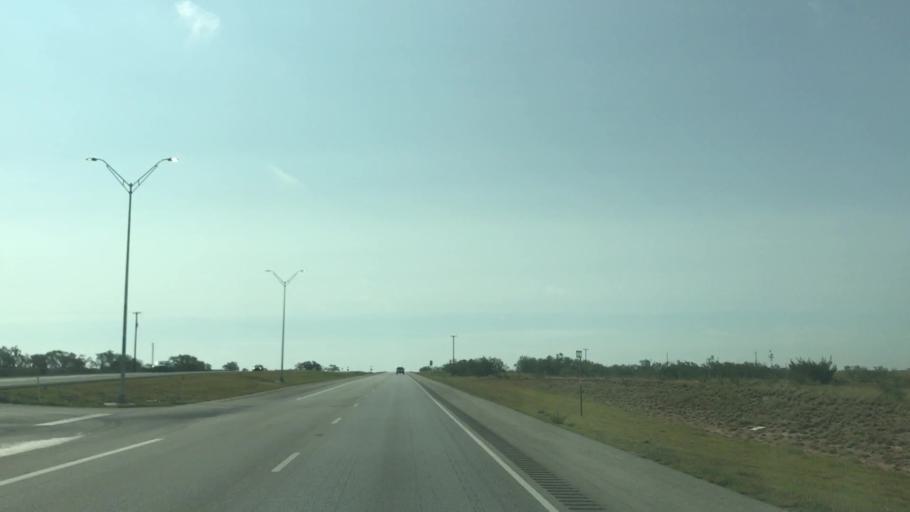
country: US
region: Texas
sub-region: Scurry County
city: Snyder
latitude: 32.6761
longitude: -100.8097
